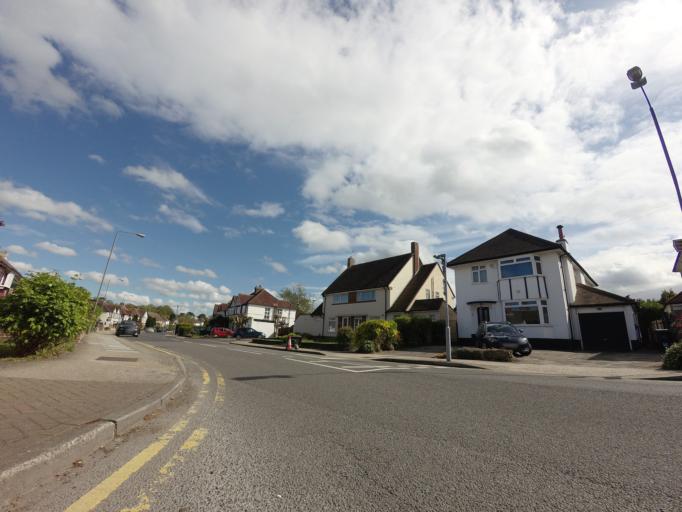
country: GB
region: England
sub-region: Greater London
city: Orpington
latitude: 51.3720
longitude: 0.1112
